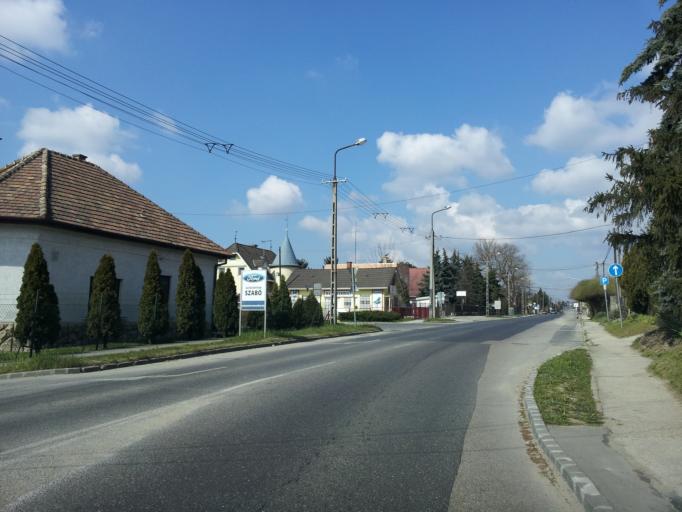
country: HU
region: Pest
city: Erd
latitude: 47.3868
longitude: 18.9246
